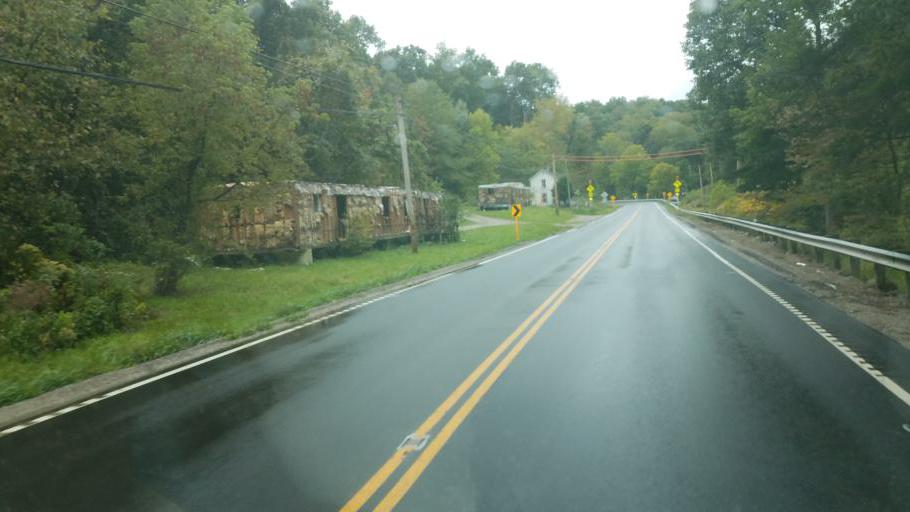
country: US
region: Ohio
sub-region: Scioto County
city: Wheelersburg
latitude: 38.7871
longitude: -82.7722
